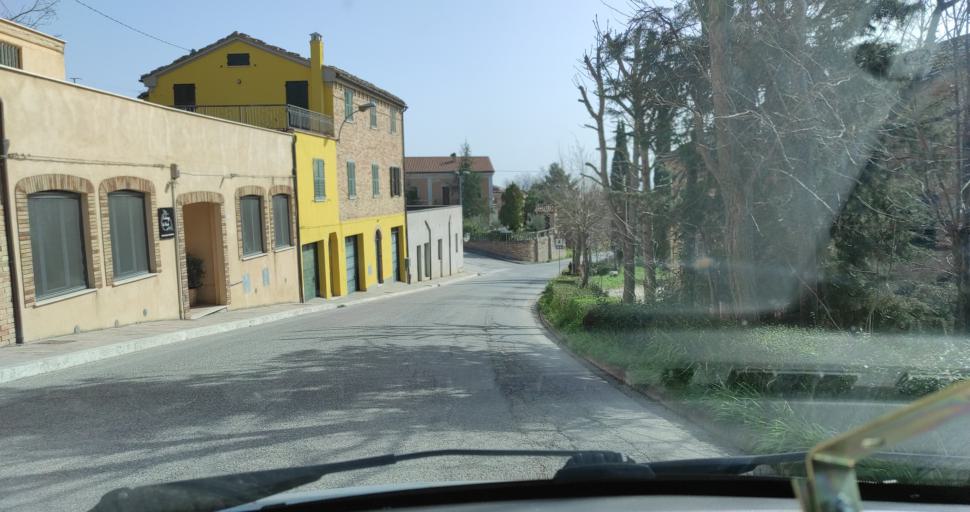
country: IT
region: The Marches
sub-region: Provincia di Macerata
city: Loro Piceno
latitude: 43.1649
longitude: 13.4176
